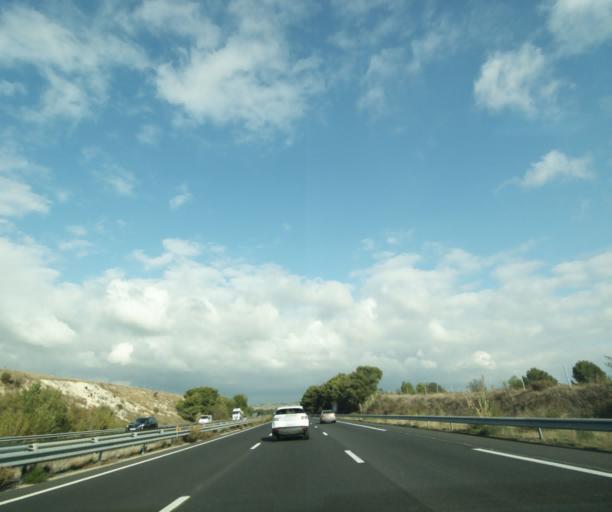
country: FR
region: Languedoc-Roussillon
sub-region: Departement de l'Aude
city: Fleury
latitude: 43.2378
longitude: 3.1423
